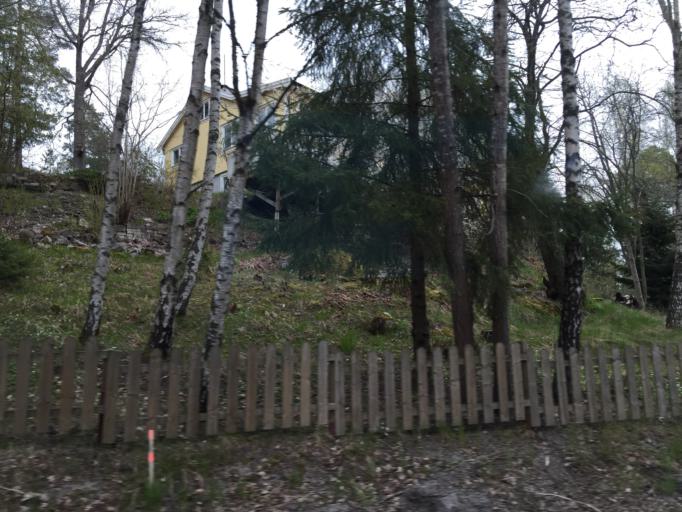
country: SE
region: Stockholm
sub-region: Salems Kommun
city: Ronninge
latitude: 59.1915
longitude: 17.7250
